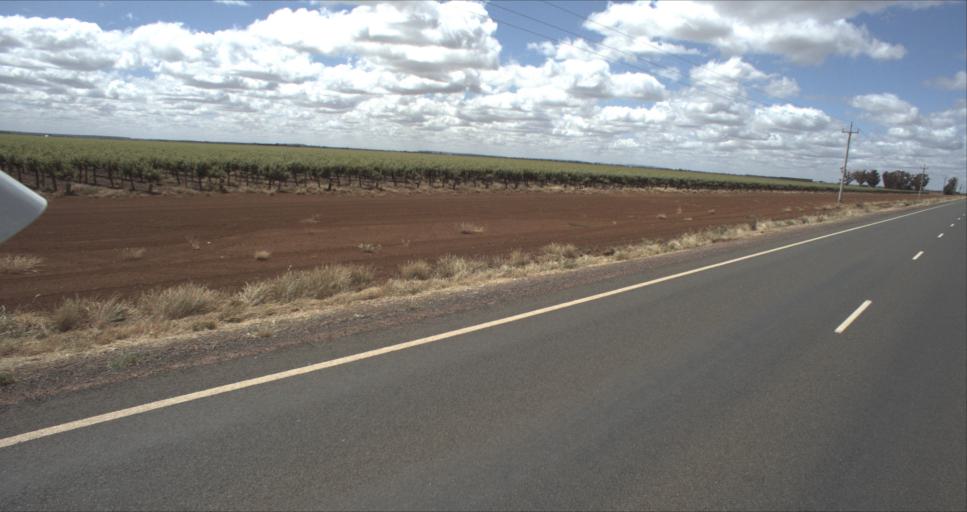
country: AU
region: New South Wales
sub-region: Murrumbidgee Shire
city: Darlington Point
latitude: -34.4701
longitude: 146.1386
